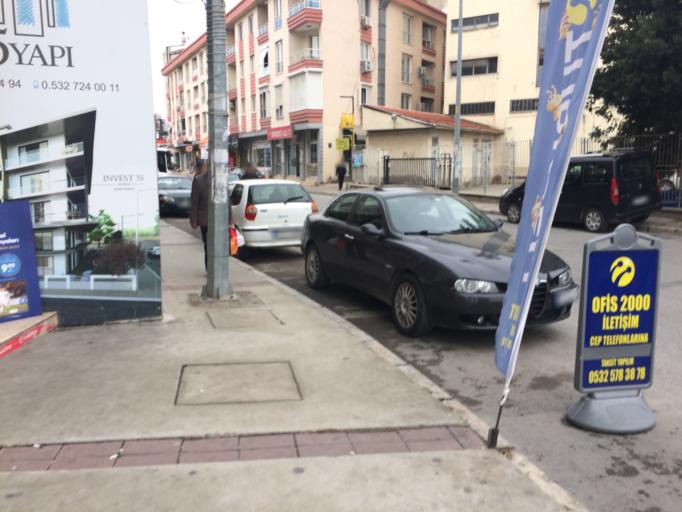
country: TR
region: Izmir
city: Karsiyaka
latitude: 38.4928
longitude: 27.0607
